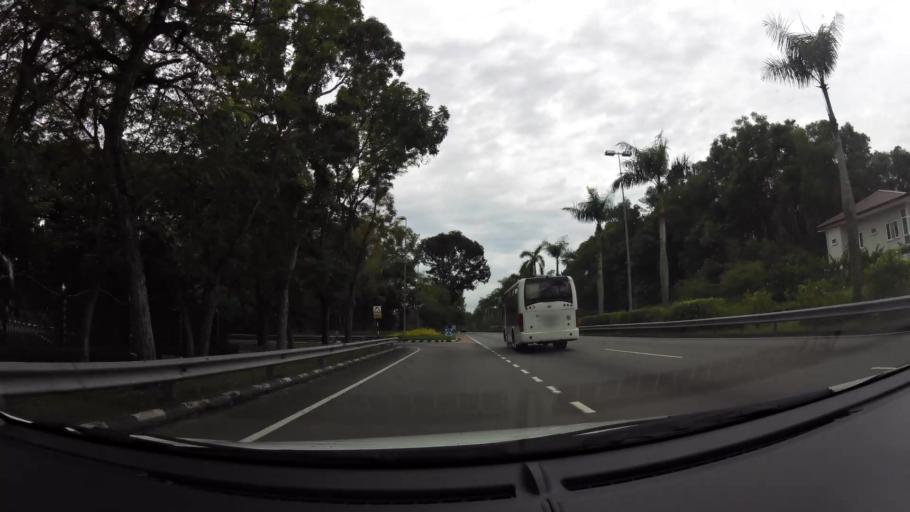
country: BN
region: Brunei and Muara
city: Bandar Seri Begawan
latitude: 4.8966
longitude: 114.9232
